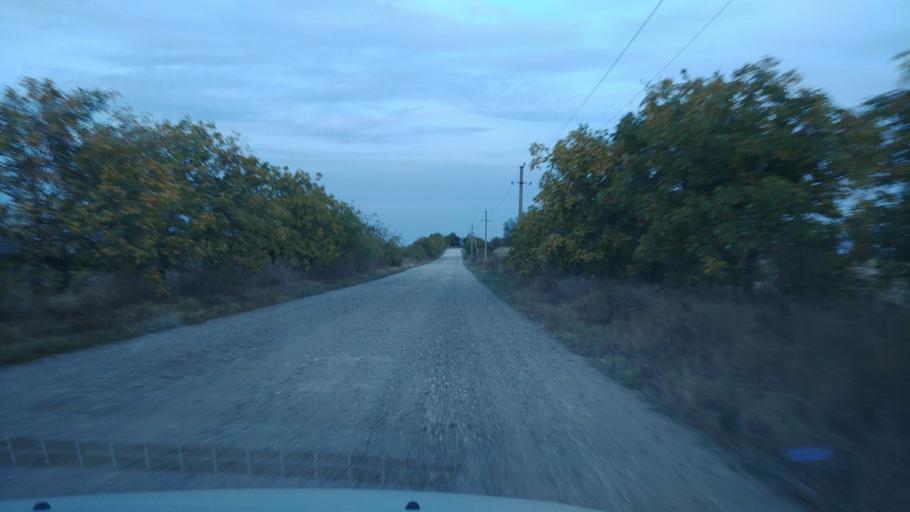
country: MD
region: Rezina
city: Saharna
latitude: 47.6811
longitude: 28.9110
